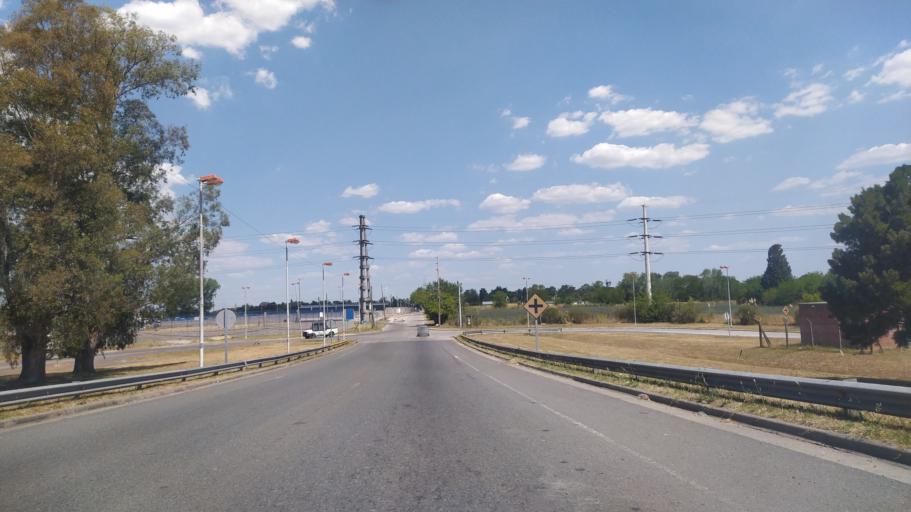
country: AR
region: Buenos Aires
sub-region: Partido de Ezeiza
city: Ezeiza
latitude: -34.9059
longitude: -58.6208
